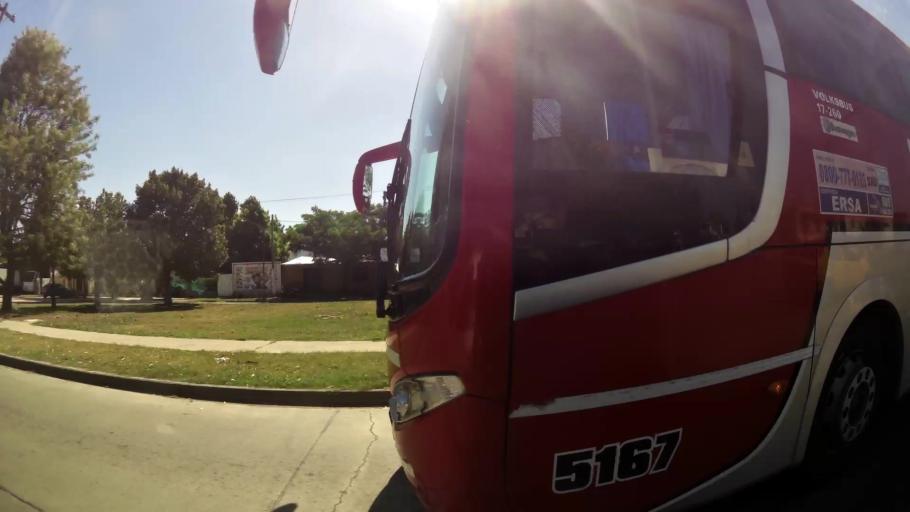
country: AR
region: Cordoba
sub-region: Departamento de Capital
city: Cordoba
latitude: -31.3759
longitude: -64.1761
